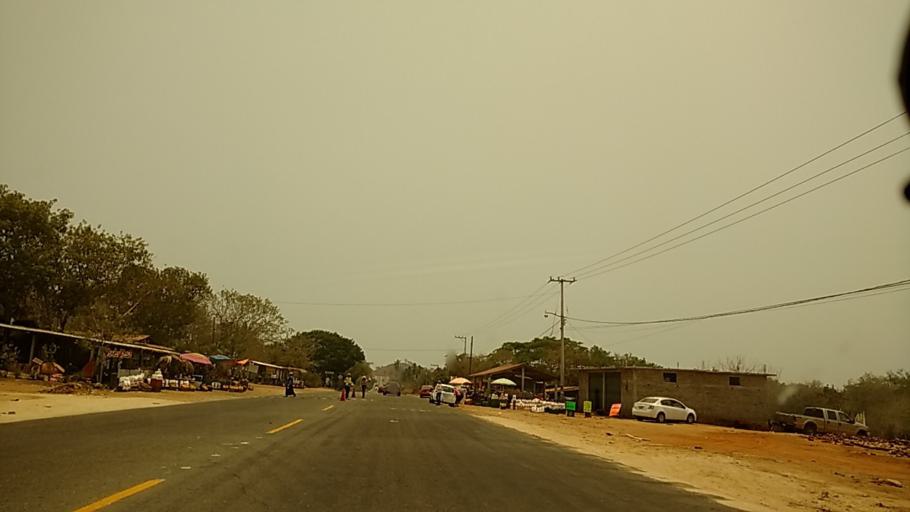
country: MX
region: Guerrero
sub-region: Atoyac de Alvarez
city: Zacualpan
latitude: 17.0816
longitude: -100.3168
